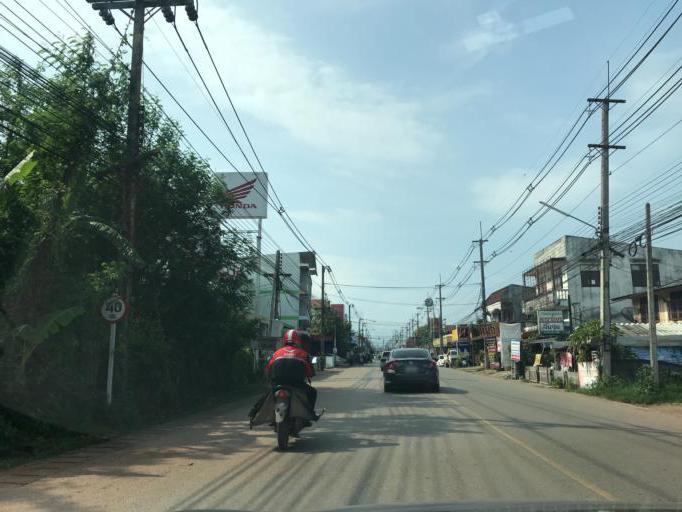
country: TH
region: Phayao
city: Chiang Kham
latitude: 19.5322
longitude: 100.3009
